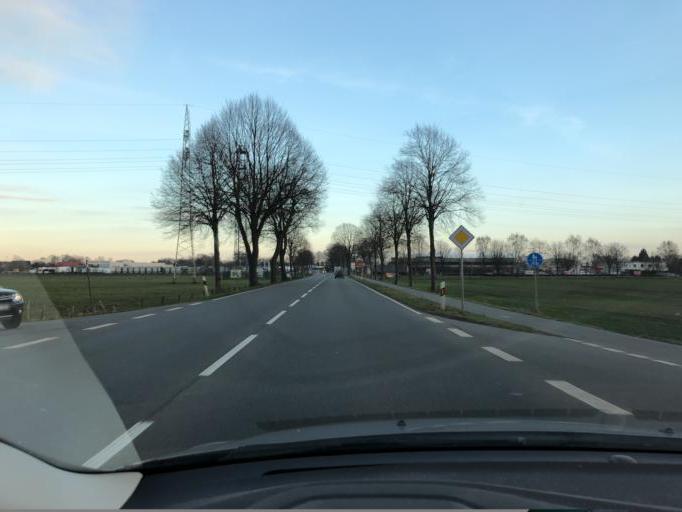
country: DE
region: Lower Saxony
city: Stuhr
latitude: 52.9895
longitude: 8.7770
